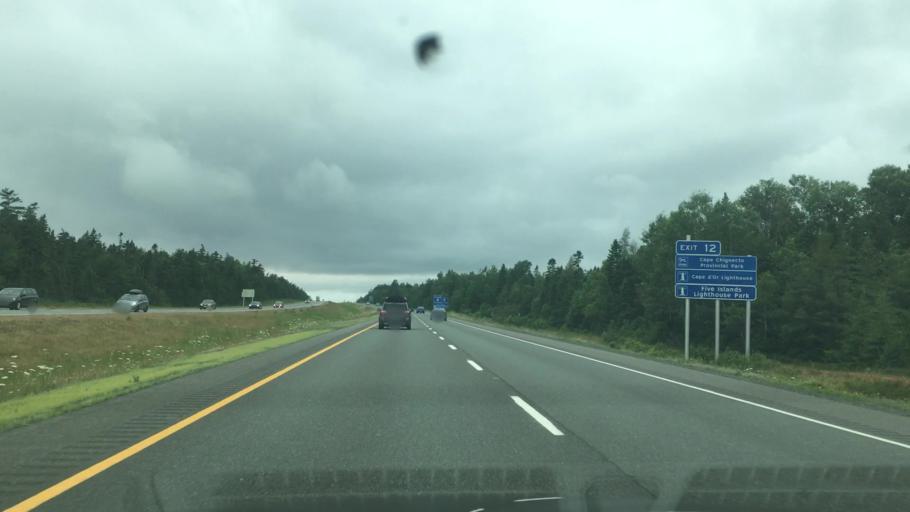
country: CA
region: Nova Scotia
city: Truro
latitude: 45.3979
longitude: -63.4633
